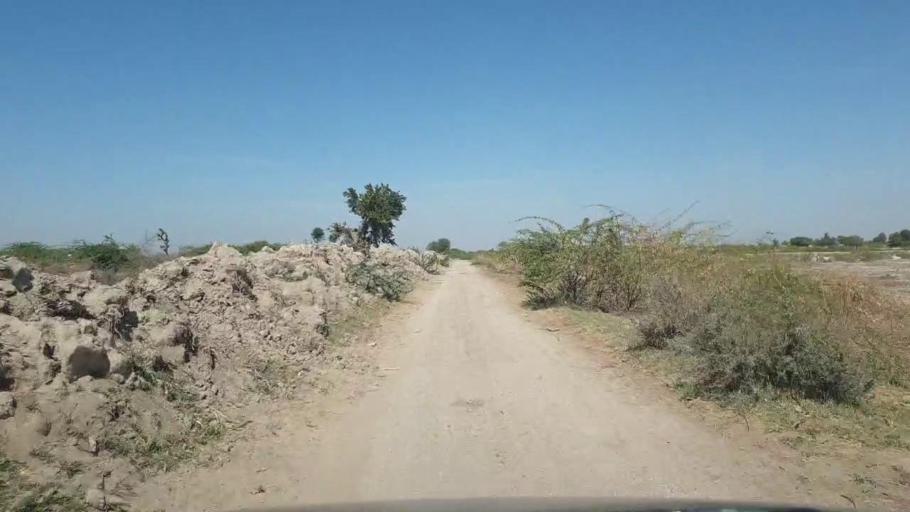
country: PK
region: Sindh
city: Dhoro Naro
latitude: 25.4060
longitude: 69.6137
